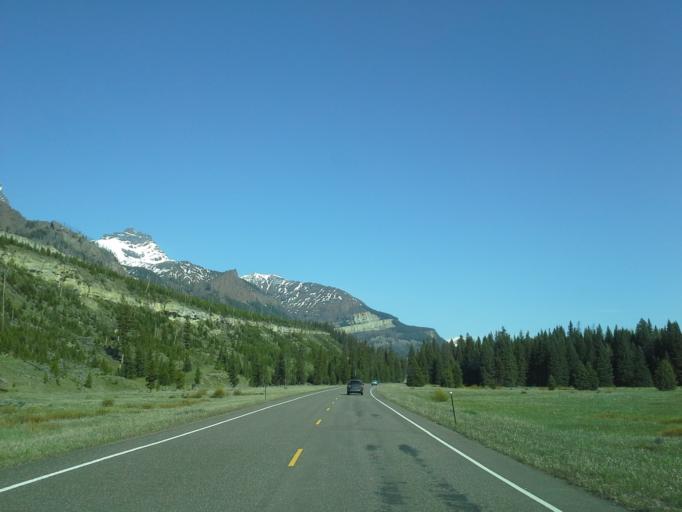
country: US
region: Montana
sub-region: Carbon County
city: Red Lodge
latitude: 44.9625
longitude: -109.8207
